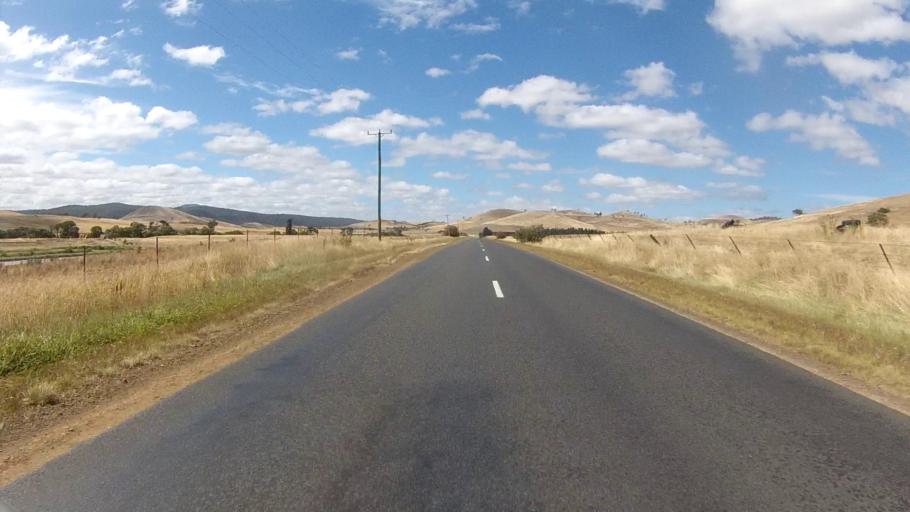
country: AU
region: Tasmania
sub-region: Brighton
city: Bridgewater
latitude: -42.5402
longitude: 147.3693
